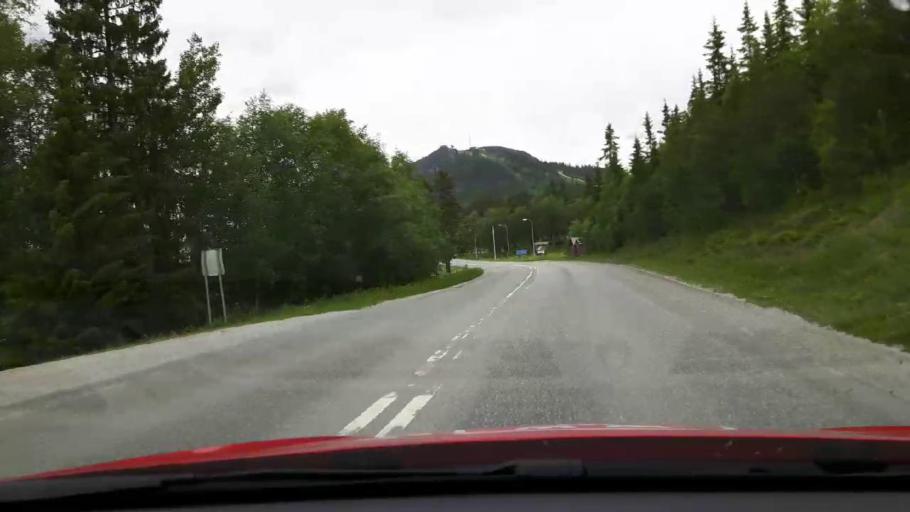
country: NO
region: Hedmark
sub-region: Engerdal
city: Engerdal
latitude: 62.5355
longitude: 12.5579
